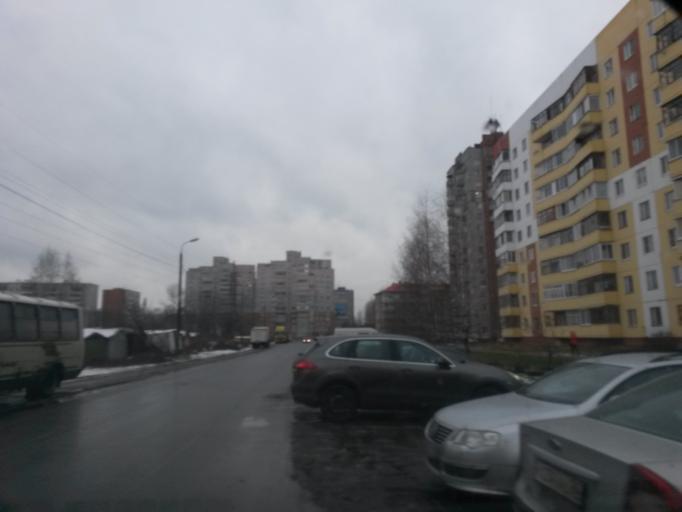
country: RU
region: Jaroslavl
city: Yaroslavl
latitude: 57.6459
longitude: 39.9597
